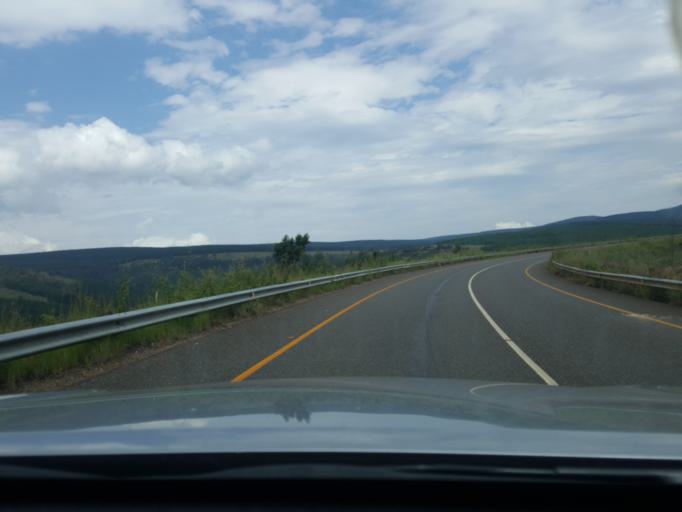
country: ZA
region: Mpumalanga
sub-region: Ehlanzeni District
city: Graksop
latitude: -25.1079
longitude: 30.8066
